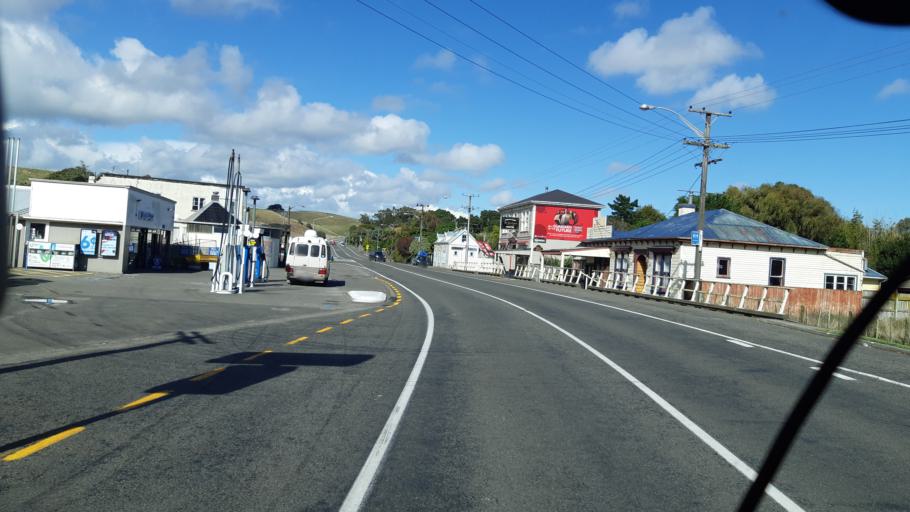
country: NZ
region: Manawatu-Wanganui
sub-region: Wanganui District
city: Wanganui
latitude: -40.0460
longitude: 175.2136
